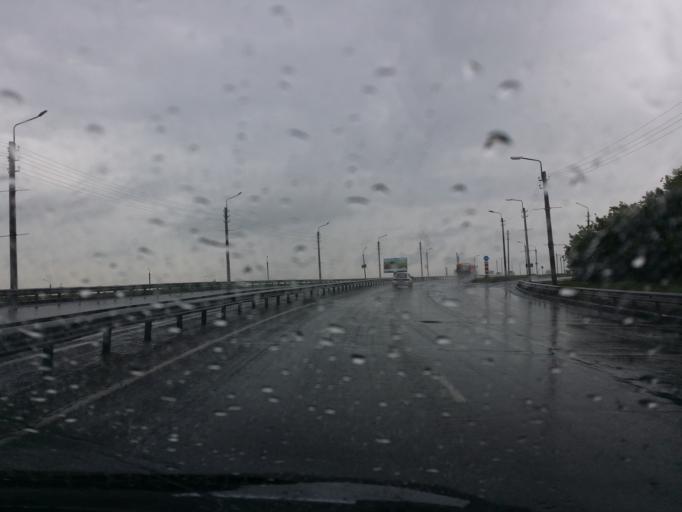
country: RU
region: Altai Krai
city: Zaton
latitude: 53.3260
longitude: 83.7949
